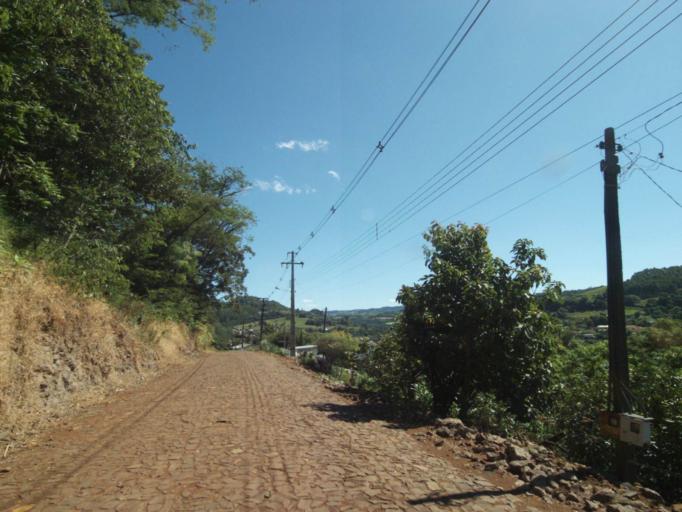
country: BR
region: Parana
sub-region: Ampere
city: Ampere
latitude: -26.1695
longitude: -53.3596
